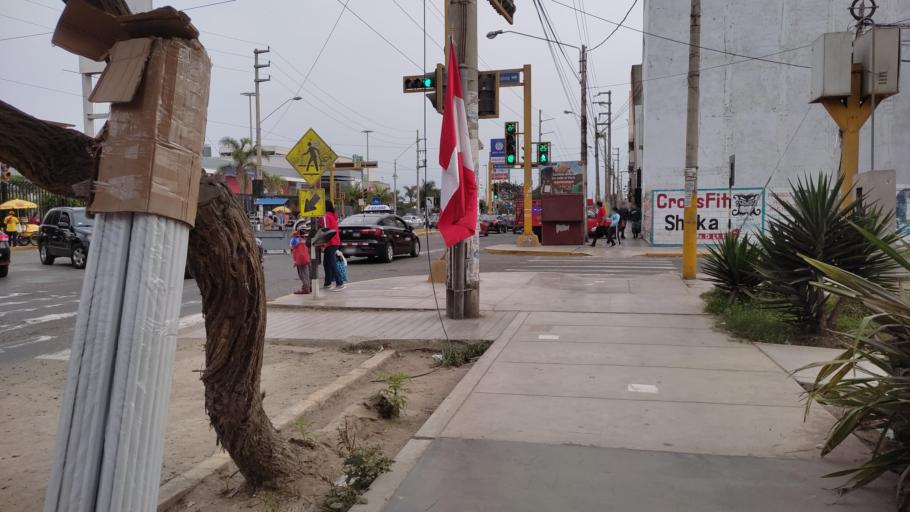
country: PE
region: La Libertad
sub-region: Provincia de Trujillo
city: Buenos Aires
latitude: -8.1297
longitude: -79.0321
